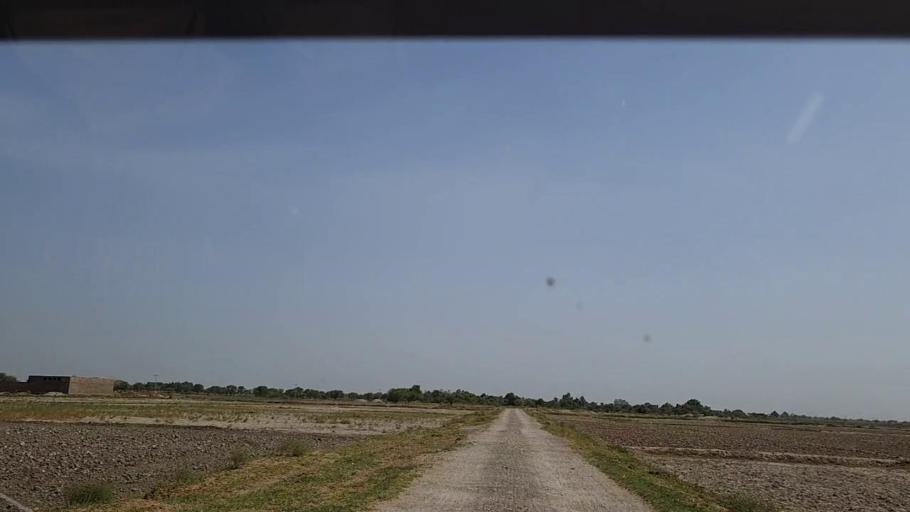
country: PK
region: Sindh
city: Phulji
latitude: 26.9501
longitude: 67.7160
